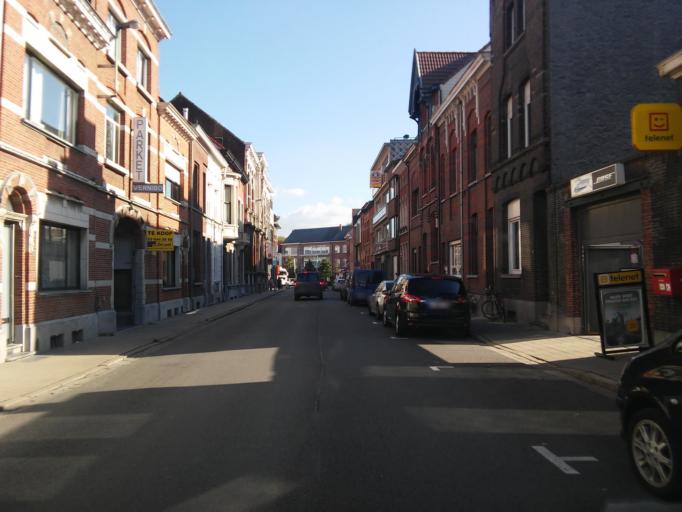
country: BE
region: Flanders
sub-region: Provincie Antwerpen
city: Boom
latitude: 51.0874
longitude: 4.3681
